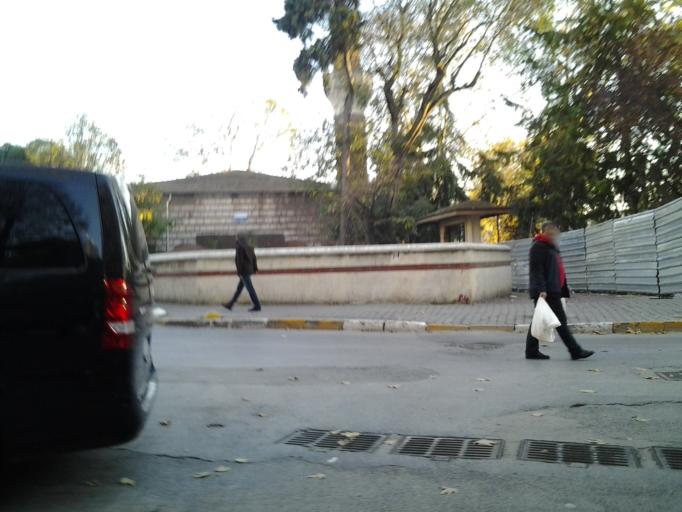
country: TR
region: Istanbul
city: Eminoenue
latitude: 41.0276
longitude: 28.9798
